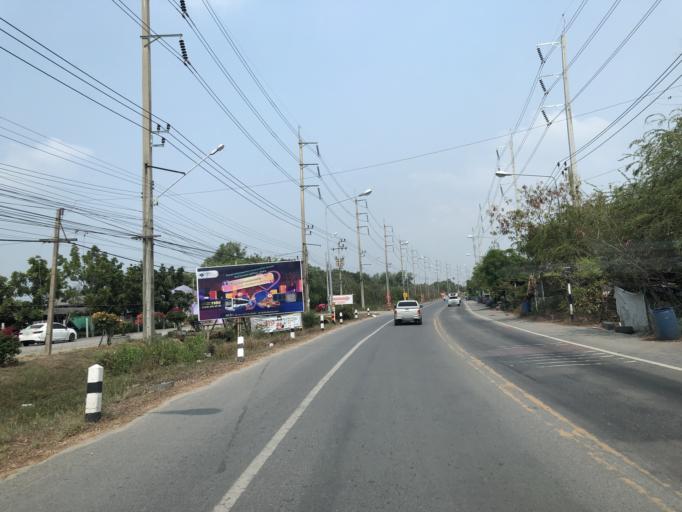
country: TH
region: Samut Prakan
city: Bang Bo
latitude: 13.5069
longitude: 100.8336
